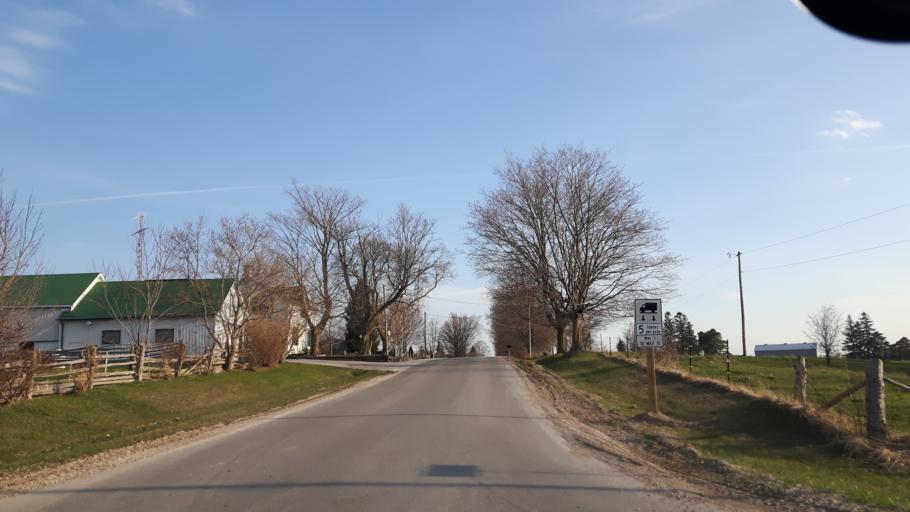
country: CA
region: Ontario
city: Goderich
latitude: 43.6428
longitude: -81.6643
